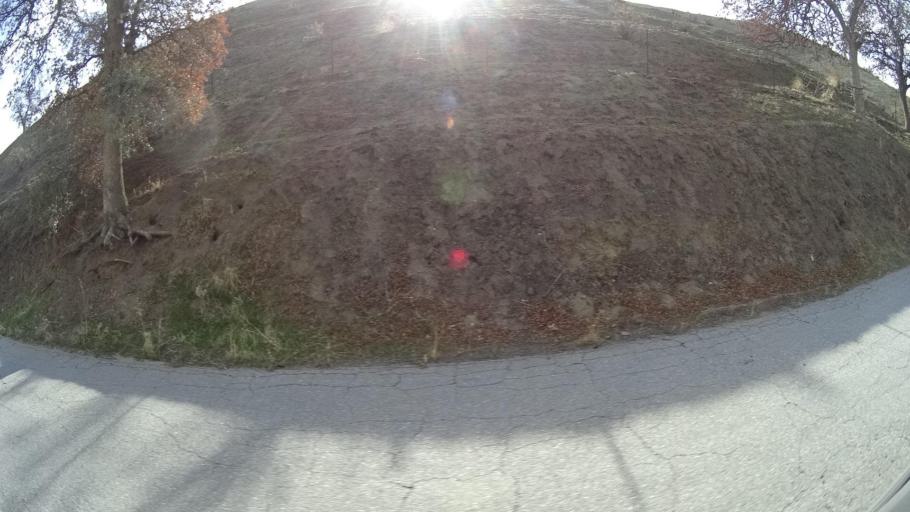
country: US
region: California
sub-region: Kern County
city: Bear Valley Springs
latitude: 35.2857
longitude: -118.6634
